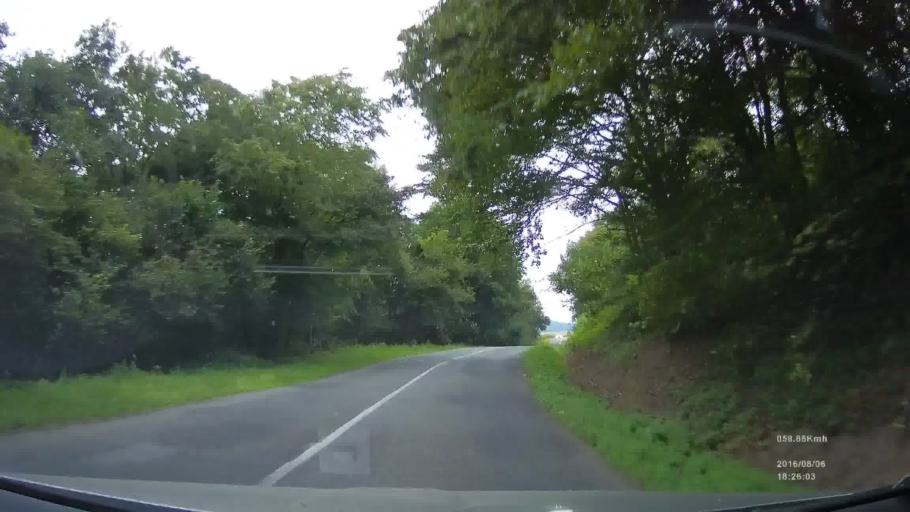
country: SK
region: Presovsky
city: Svidnik
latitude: 49.2884
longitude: 21.5714
